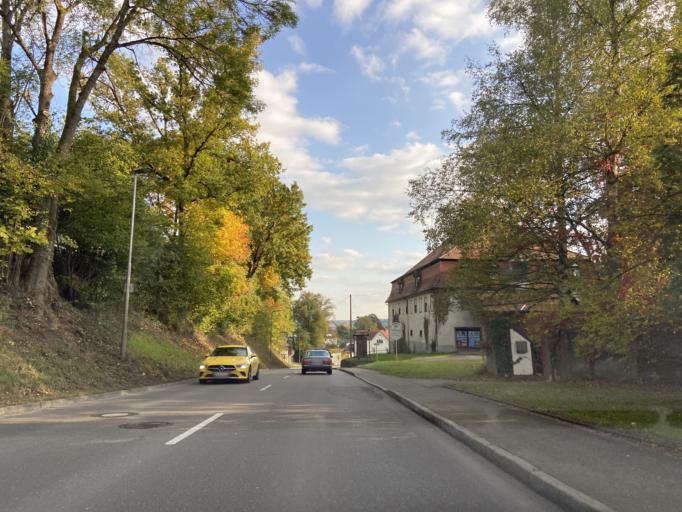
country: DE
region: Baden-Wuerttemberg
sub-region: Tuebingen Region
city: Scheer
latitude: 48.0762
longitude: 9.2958
